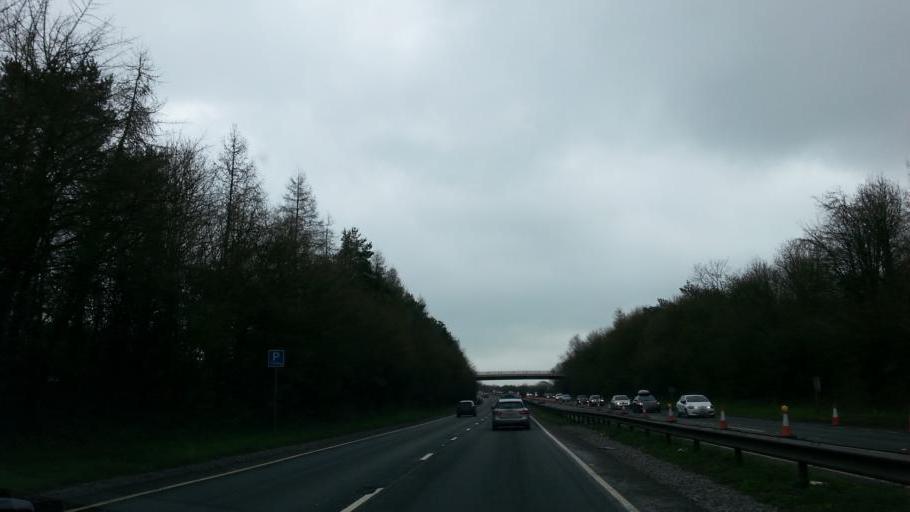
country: GB
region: England
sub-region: Devon
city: Cullompton
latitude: 50.9193
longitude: -3.4150
